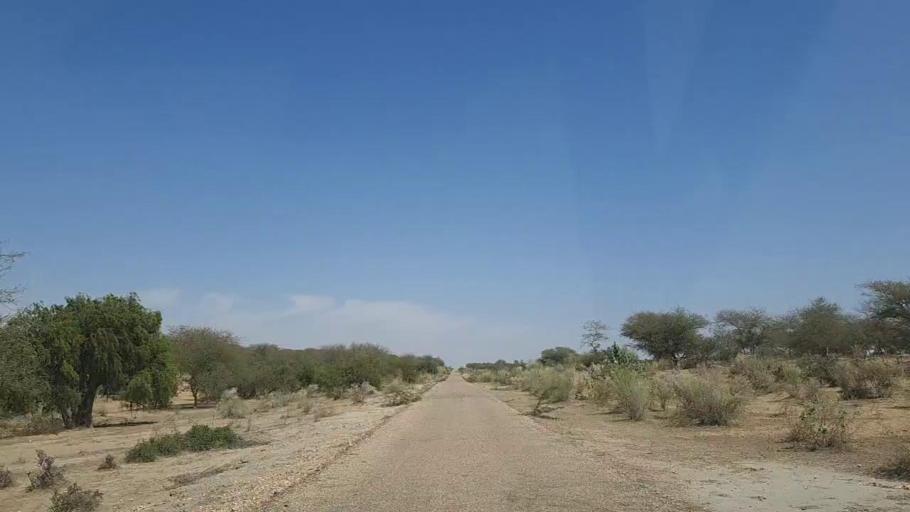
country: PK
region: Sindh
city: Mithi
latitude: 24.8288
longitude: 69.7082
